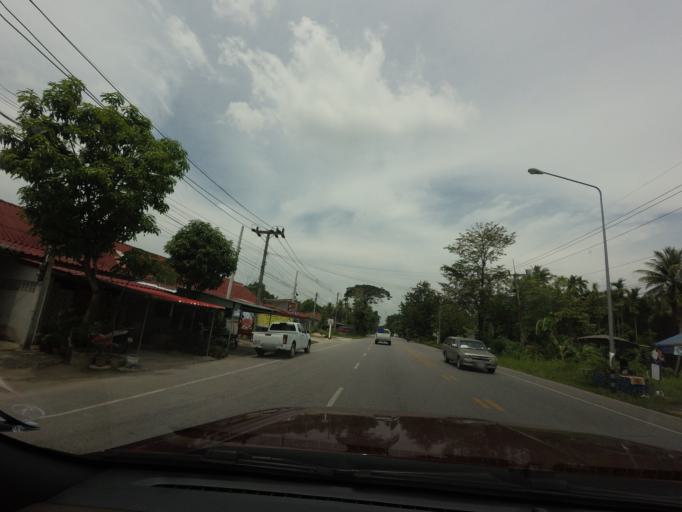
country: TH
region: Pattani
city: Mae Lan
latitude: 6.6181
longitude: 101.3058
